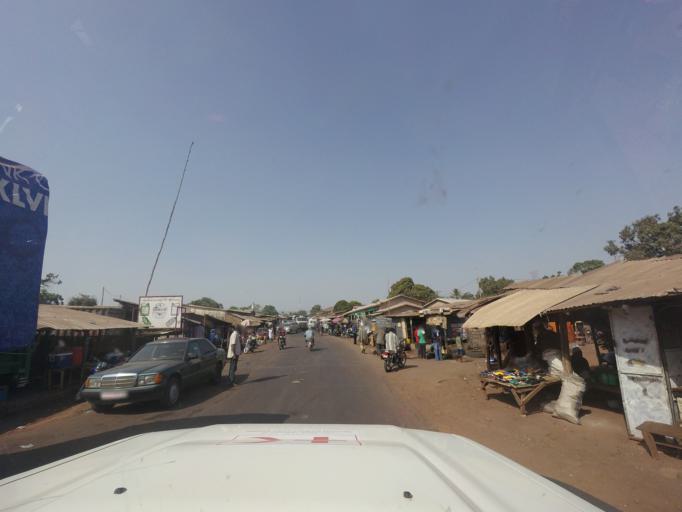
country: GN
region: Mamou
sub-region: Mamou Prefecture
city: Mamou
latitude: 10.2798
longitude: -12.4405
